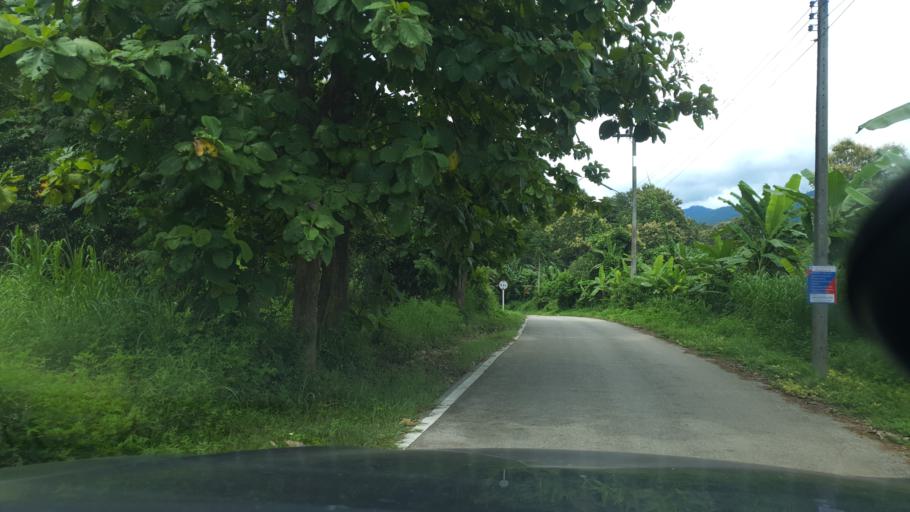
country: TH
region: Lampang
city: Hang Chat
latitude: 18.4249
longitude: 99.2649
